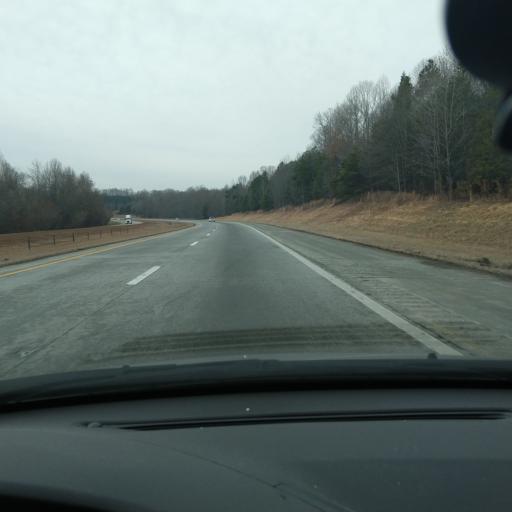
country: US
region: North Carolina
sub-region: Davidson County
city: Welcome
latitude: 35.8710
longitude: -80.2594
